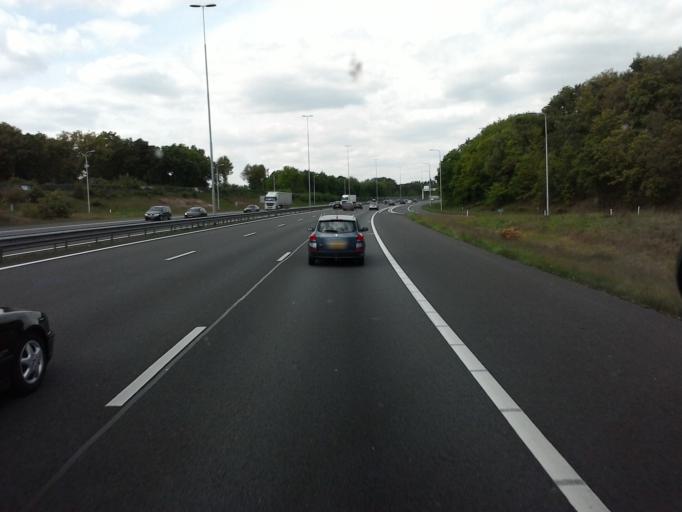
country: NL
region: Gelderland
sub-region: Gemeente Renkum
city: Heelsum
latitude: 51.9760
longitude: 5.7631
